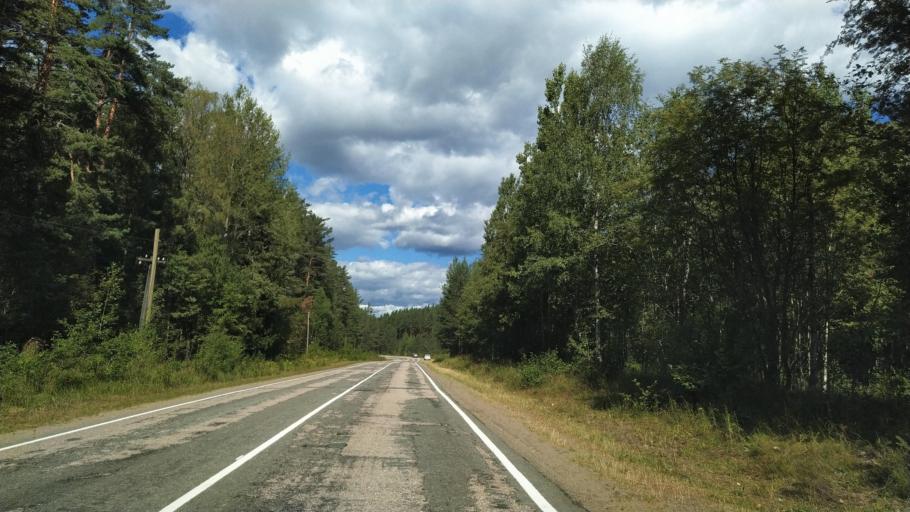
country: RU
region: Leningrad
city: Priozersk
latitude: 60.9933
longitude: 30.2562
